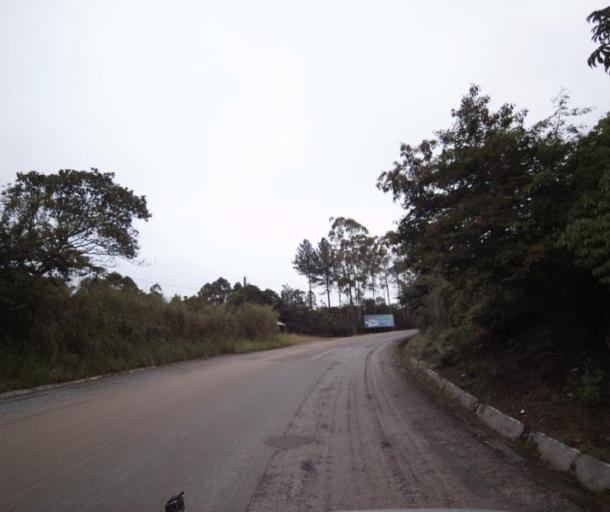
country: BR
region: Goias
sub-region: Pirenopolis
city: Pirenopolis
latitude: -15.9192
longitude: -48.8096
